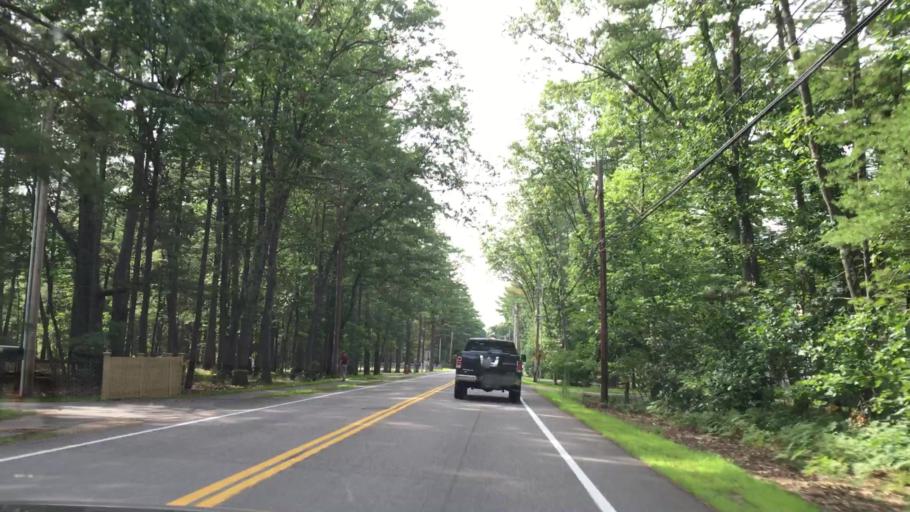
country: US
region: New Hampshire
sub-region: Merrimack County
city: East Concord
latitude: 43.2317
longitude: -71.5184
